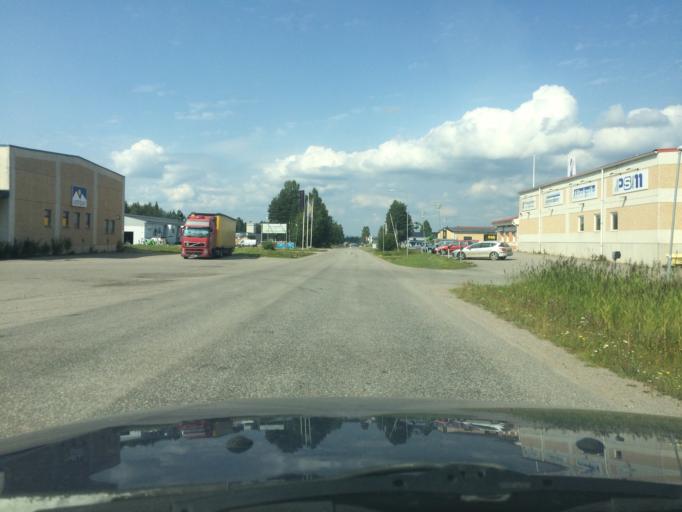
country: SE
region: Norrbotten
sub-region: Pitea Kommun
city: Bergsviken
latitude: 65.3318
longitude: 21.4261
